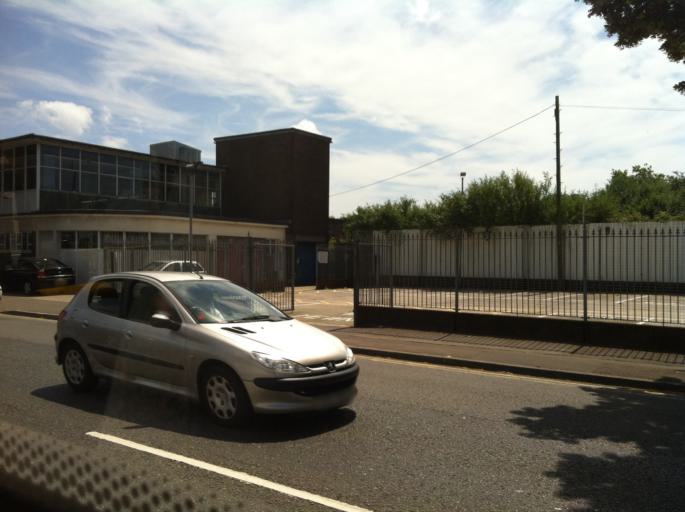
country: GB
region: Wales
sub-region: Cardiff
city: Cardiff
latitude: 51.4840
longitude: -3.2243
